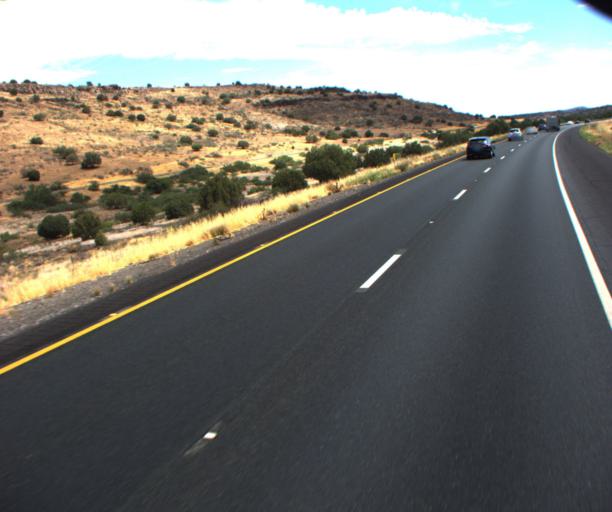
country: US
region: Arizona
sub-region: Yavapai County
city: Camp Verde
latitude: 34.4817
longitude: -112.0174
